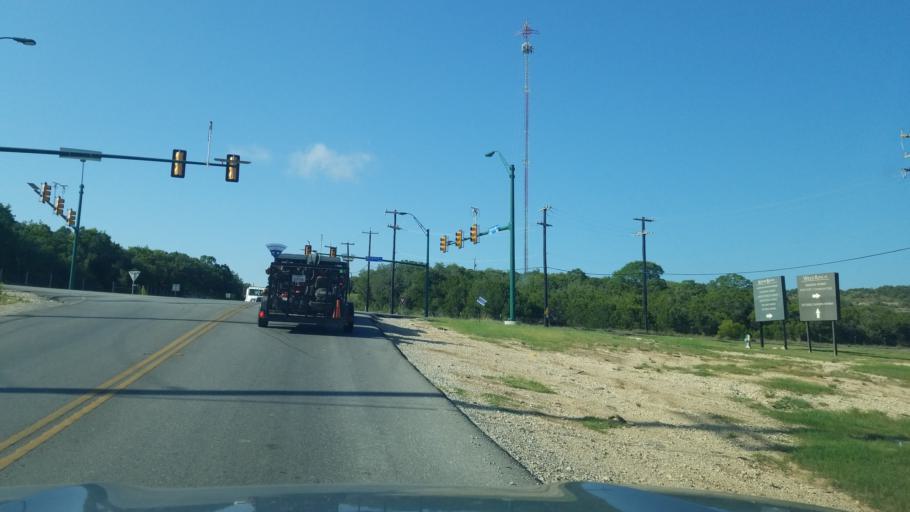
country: US
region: Texas
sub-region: Bexar County
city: Timberwood Park
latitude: 29.7145
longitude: -98.4544
